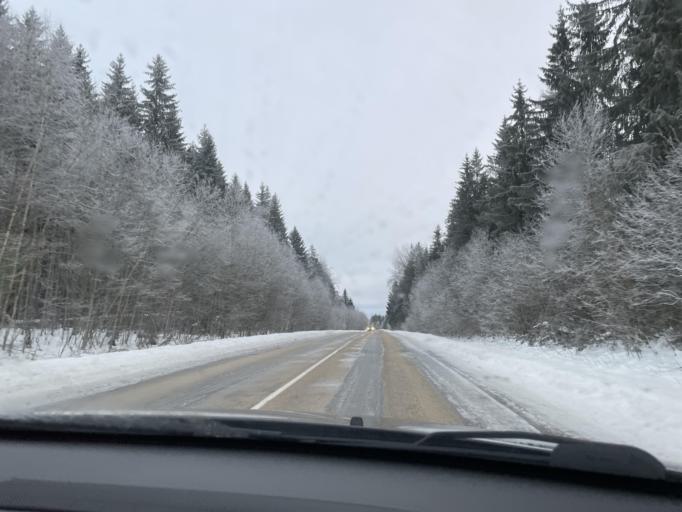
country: LV
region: Rezekne
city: Rezekne
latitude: 56.4997
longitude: 27.3847
